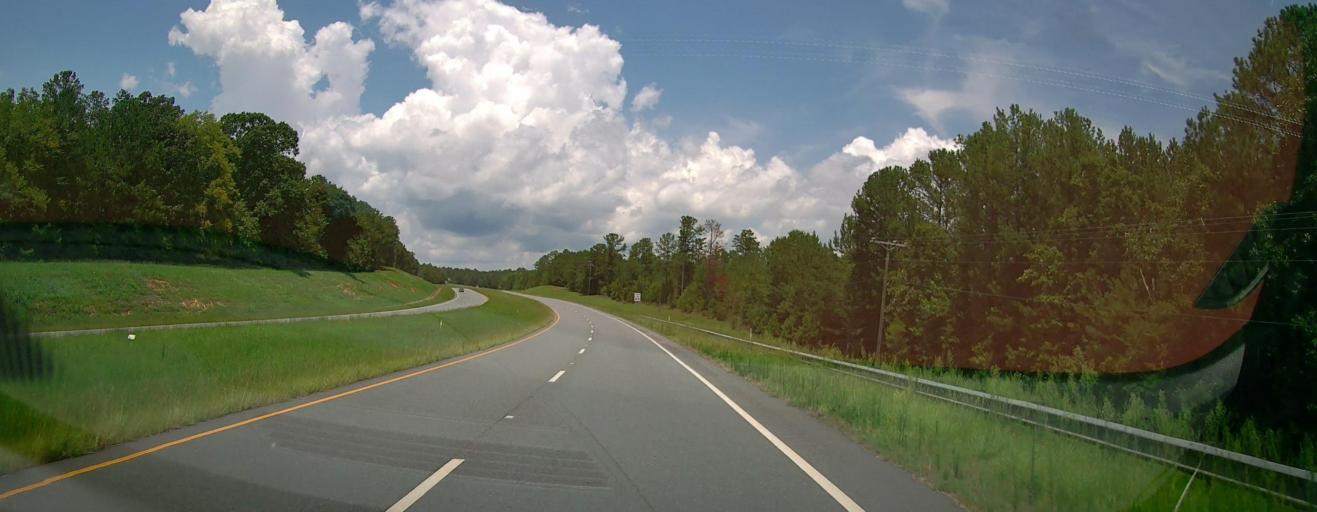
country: US
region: Georgia
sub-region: Upson County
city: Thomaston
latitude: 32.7633
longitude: -84.2443
